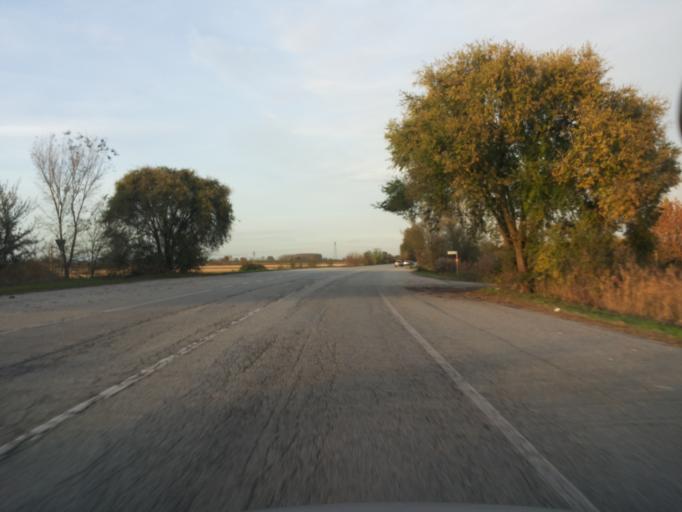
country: IT
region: Piedmont
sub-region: Provincia di Vercelli
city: Tricerro
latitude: 45.2213
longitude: 8.3097
